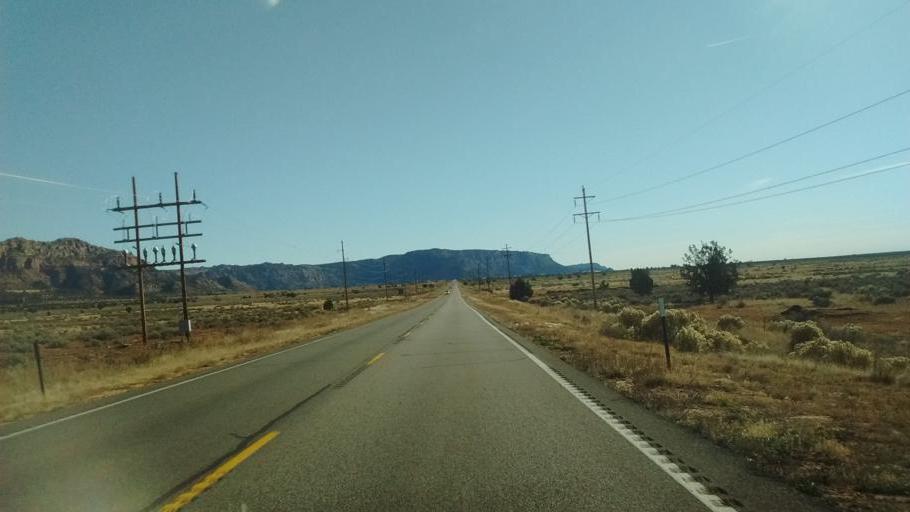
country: US
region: Arizona
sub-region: Mohave County
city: Colorado City
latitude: 37.0185
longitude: -113.0319
